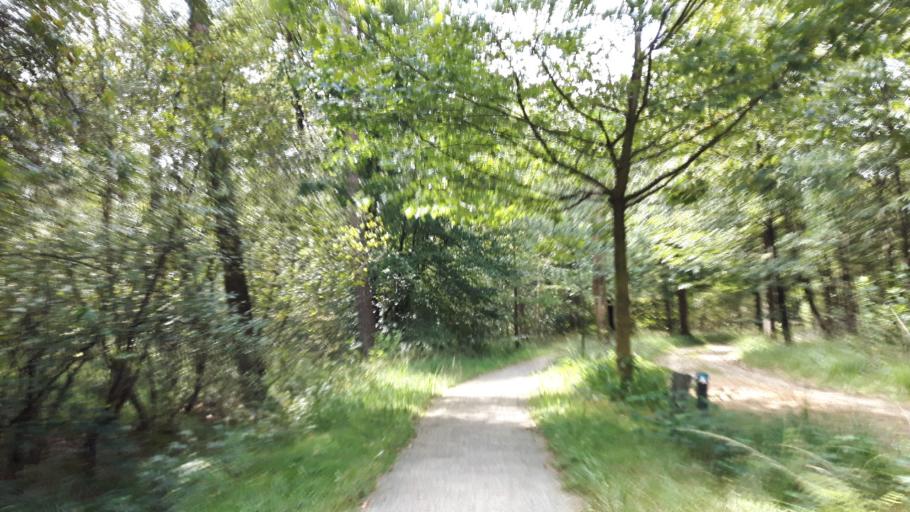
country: NL
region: Friesland
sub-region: Gemeente Smallingerland
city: Drachtstercompagnie
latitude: 53.0710
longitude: 6.2074
